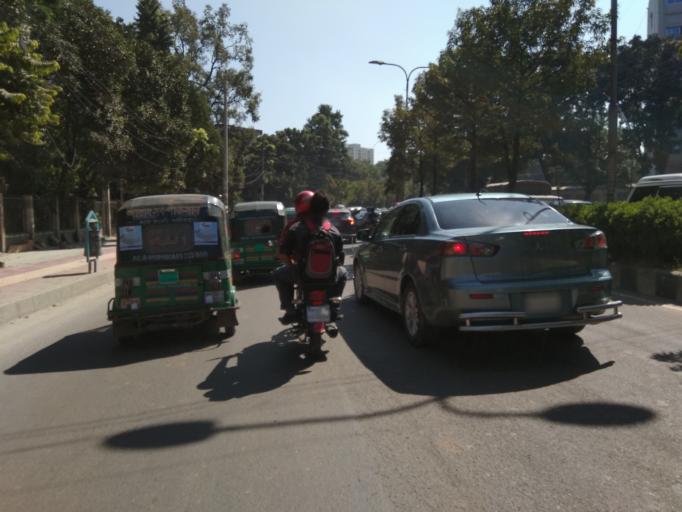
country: BD
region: Dhaka
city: Paltan
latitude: 23.7444
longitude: 90.4050
